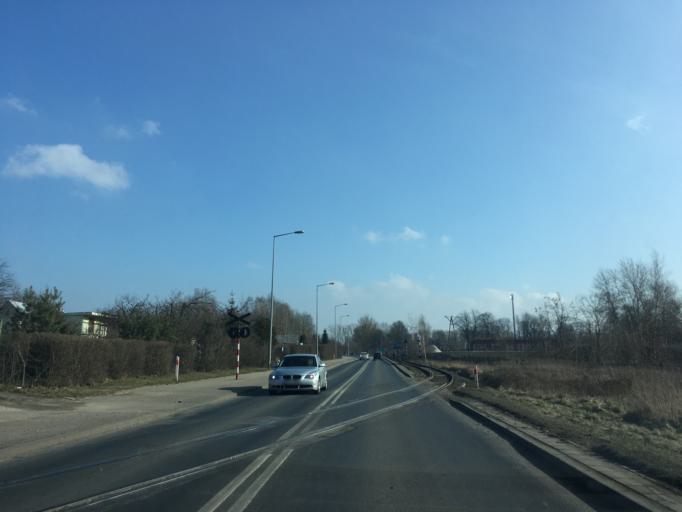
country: PL
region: Lower Silesian Voivodeship
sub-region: Powiat boleslawiecki
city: Boleslawiec
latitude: 51.2694
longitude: 15.5717
